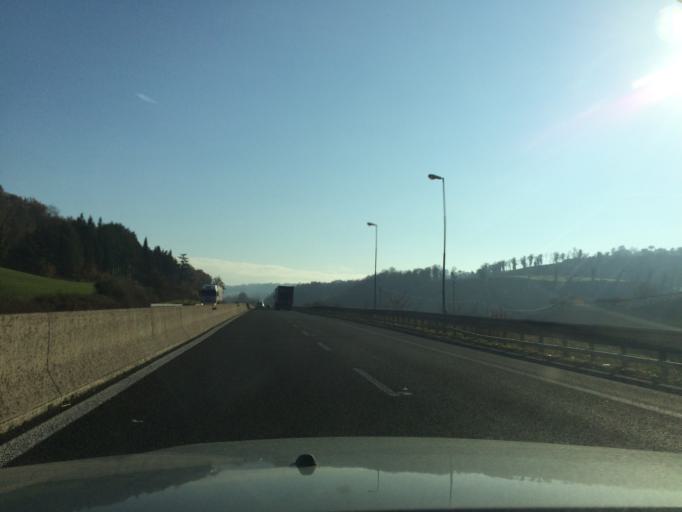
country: IT
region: Umbria
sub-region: Provincia di Perugia
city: Todi
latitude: 42.7719
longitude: 12.4482
